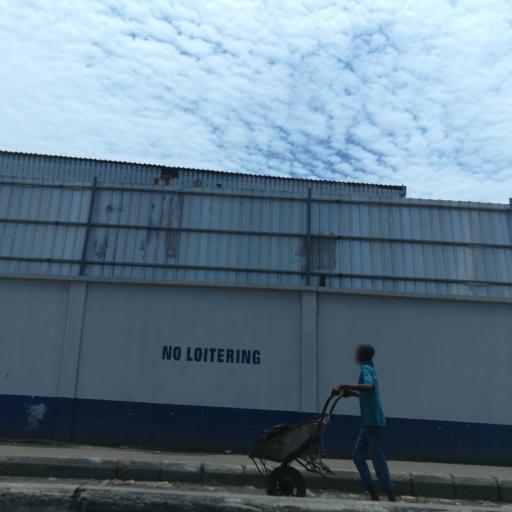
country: NG
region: Lagos
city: Ebute Metta
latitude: 6.4683
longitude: 3.3817
